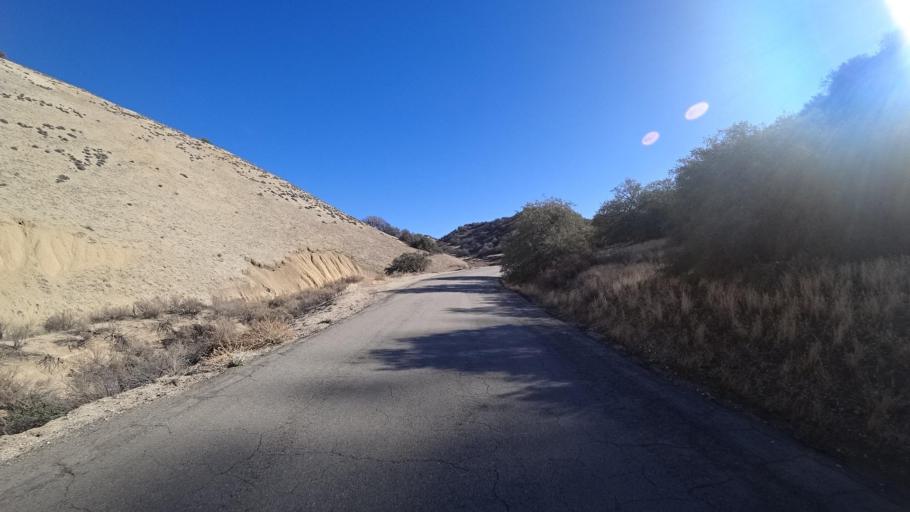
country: US
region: California
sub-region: Kern County
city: Maricopa
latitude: 34.9479
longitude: -119.4022
